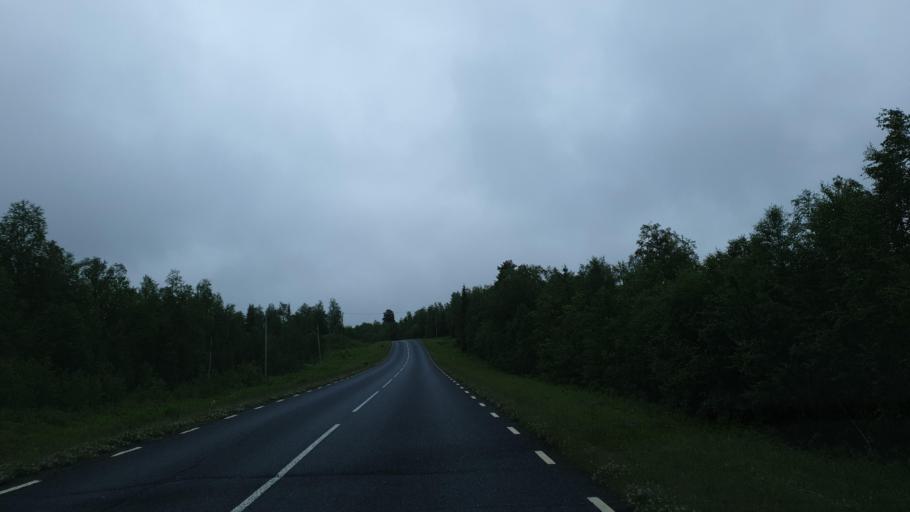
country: SE
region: Vaesterbotten
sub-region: Vilhelmina Kommun
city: Sjoberg
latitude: 65.2530
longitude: 15.7262
